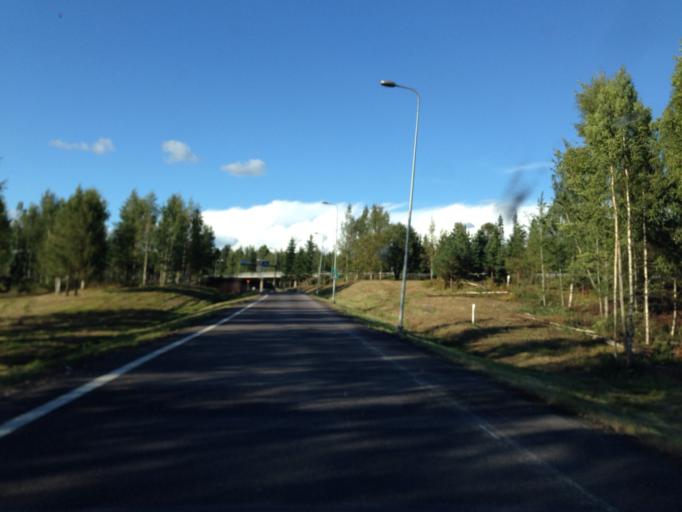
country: FI
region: Uusimaa
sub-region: Helsinki
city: Vantaa
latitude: 60.3398
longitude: 25.0018
